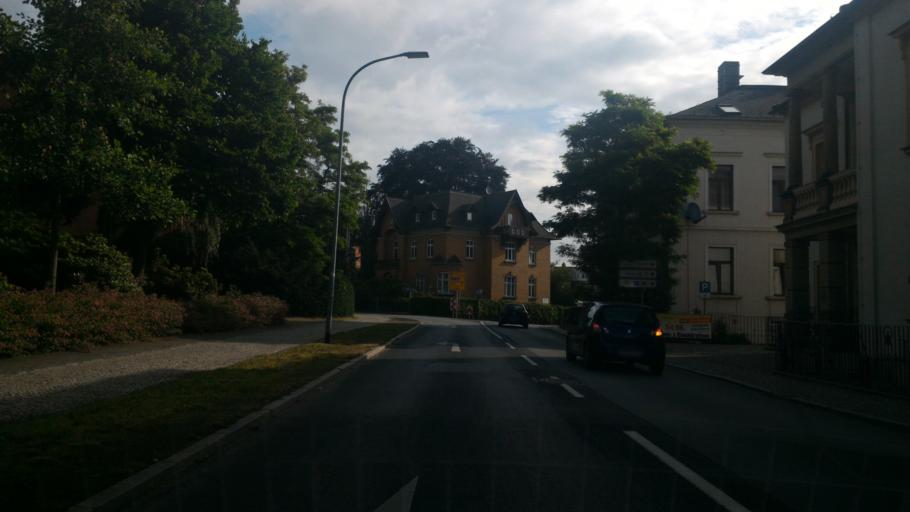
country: DE
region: Saxony
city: Zittau
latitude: 50.8953
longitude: 14.8124
